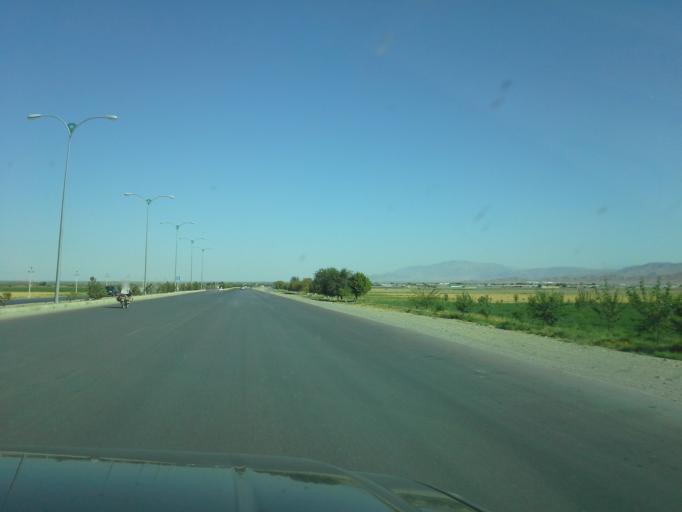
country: TM
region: Ahal
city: Baharly
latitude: 38.4161
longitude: 57.4484
